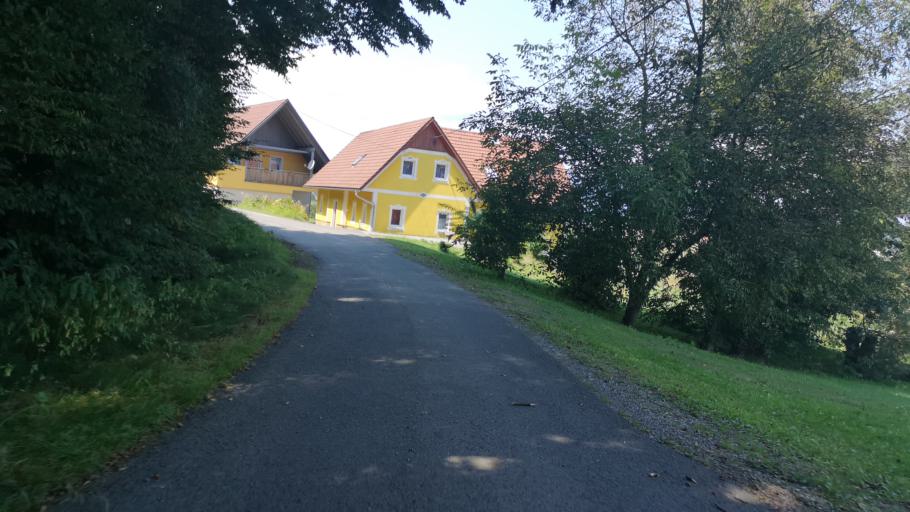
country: AT
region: Styria
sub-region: Politischer Bezirk Deutschlandsberg
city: Unterbergla
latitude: 46.8123
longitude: 15.2798
